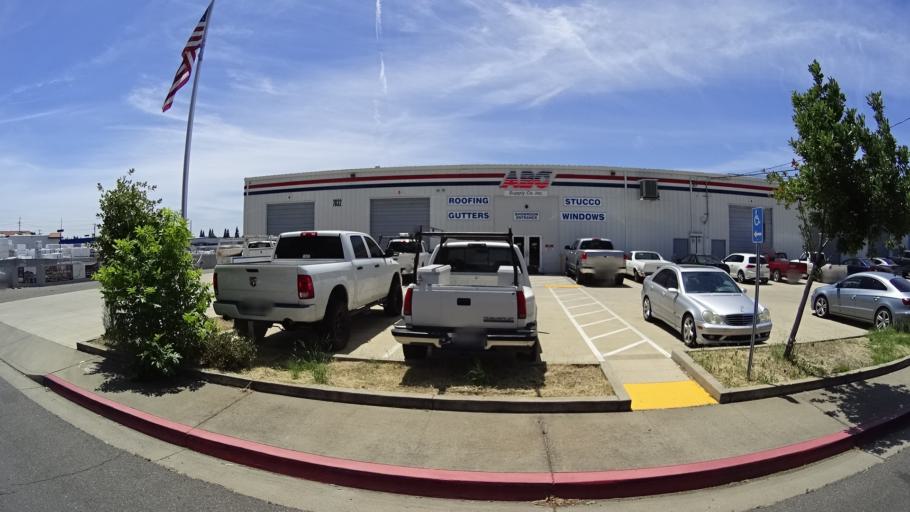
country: US
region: California
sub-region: Sacramento County
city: Florin
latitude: 38.5422
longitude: -121.4116
